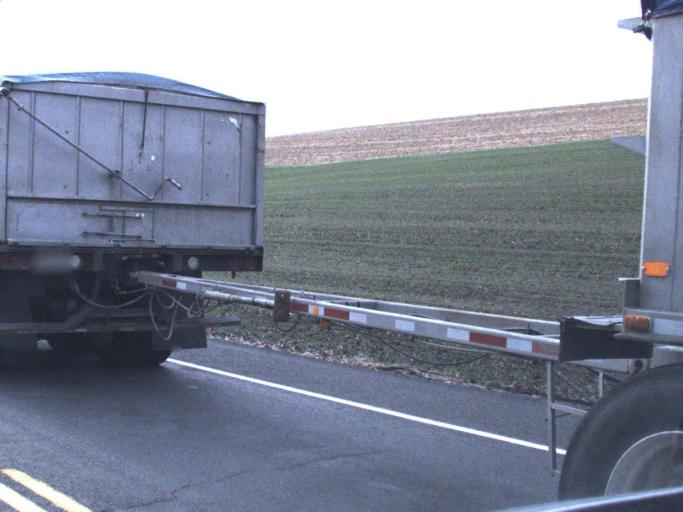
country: US
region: Washington
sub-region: Whitman County
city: Colfax
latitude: 46.8203
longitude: -117.5312
